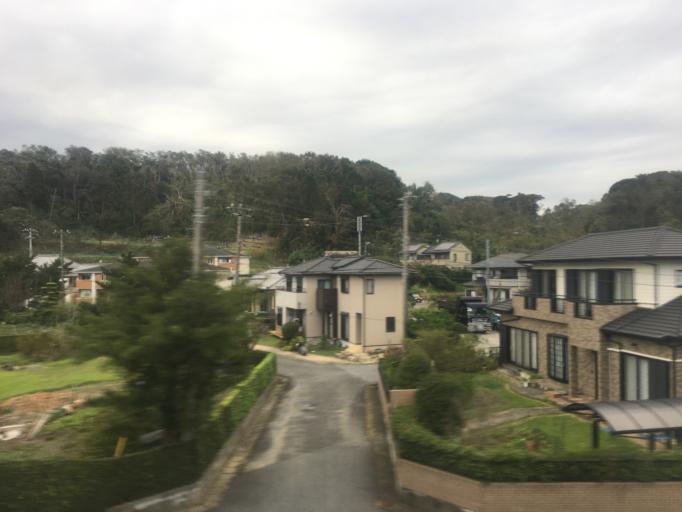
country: JP
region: Chiba
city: Kisarazu
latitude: 35.3586
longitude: 139.9207
